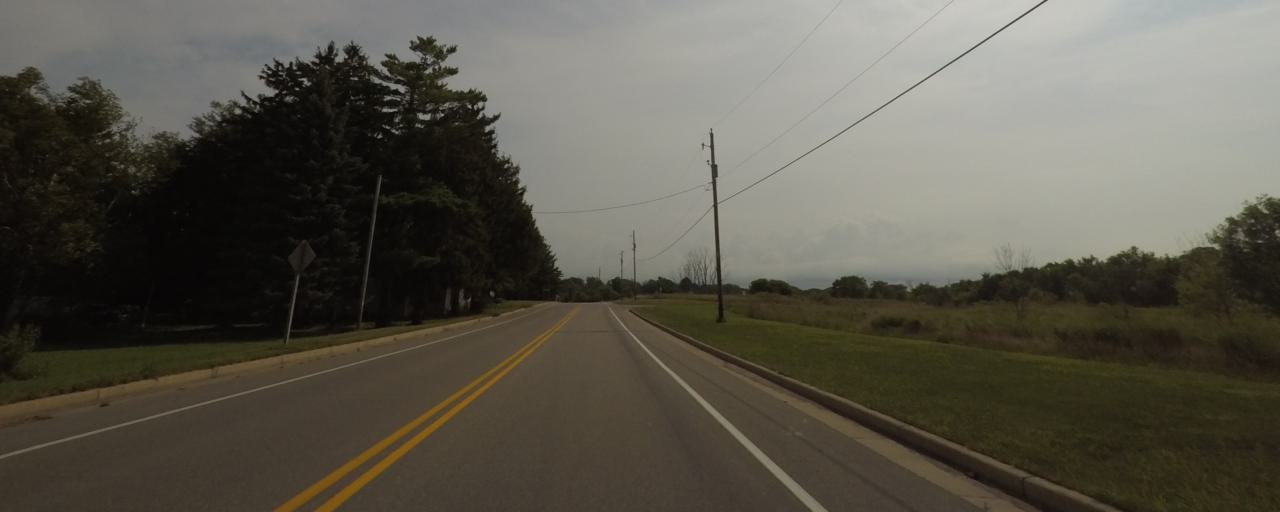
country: US
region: Wisconsin
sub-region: Jefferson County
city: Jefferson
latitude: 42.9943
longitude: -88.8308
